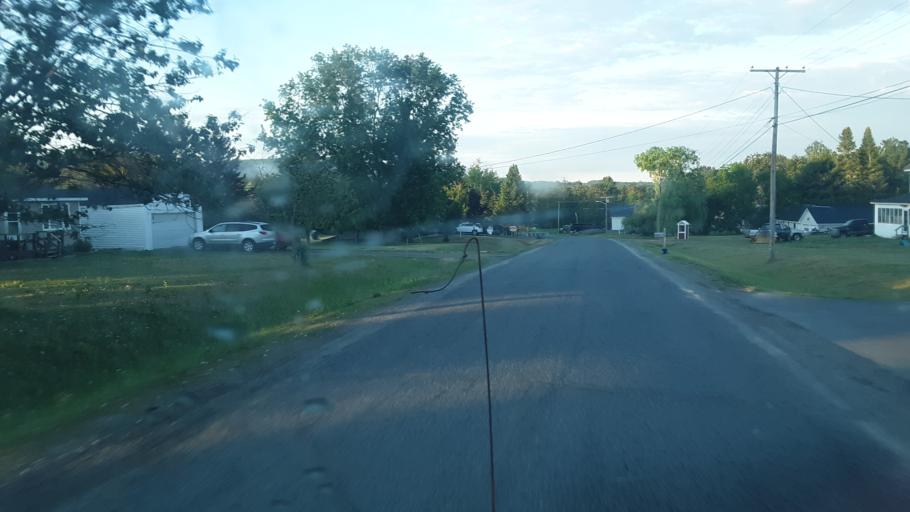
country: US
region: Maine
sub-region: Aroostook County
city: Presque Isle
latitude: 46.7578
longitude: -68.1022
